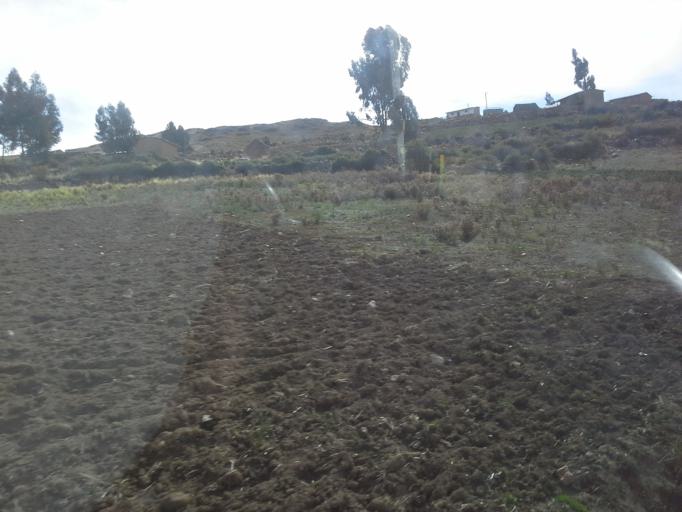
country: BO
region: Cochabamba
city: Colomi
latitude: -17.4390
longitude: -65.8345
